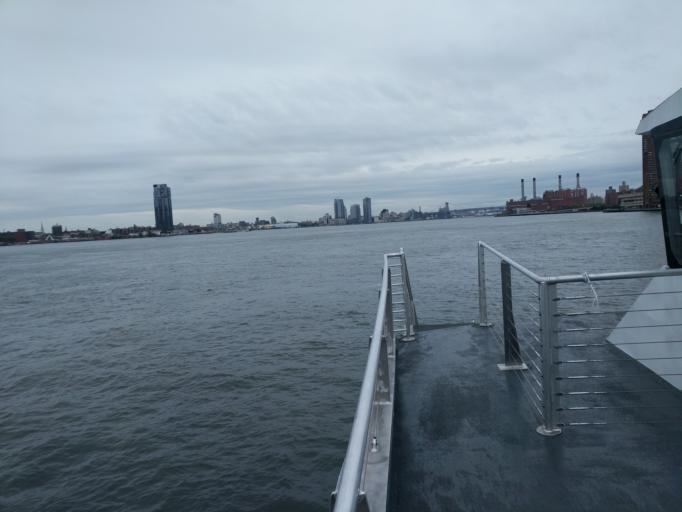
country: US
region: New York
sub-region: Queens County
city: Long Island City
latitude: 40.7442
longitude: -73.9688
